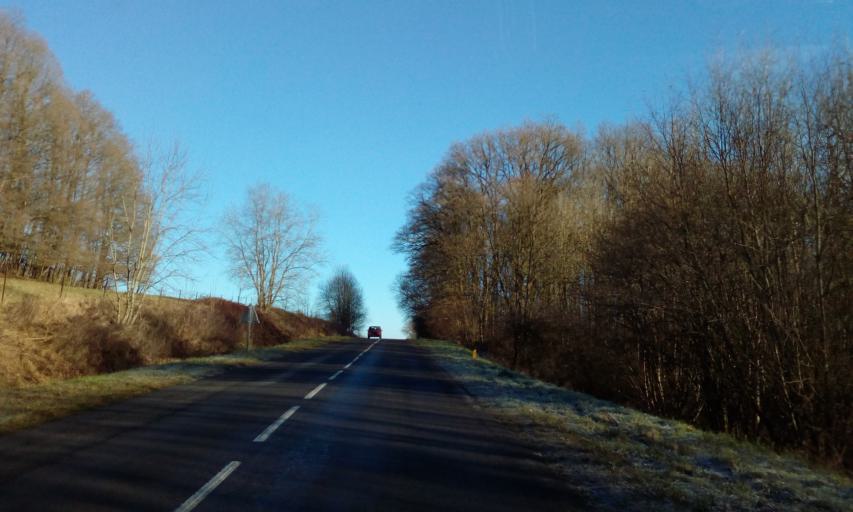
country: FR
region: Champagne-Ardenne
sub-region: Departement des Ardennes
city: Signy-le-Petit
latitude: 49.7772
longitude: 4.3598
